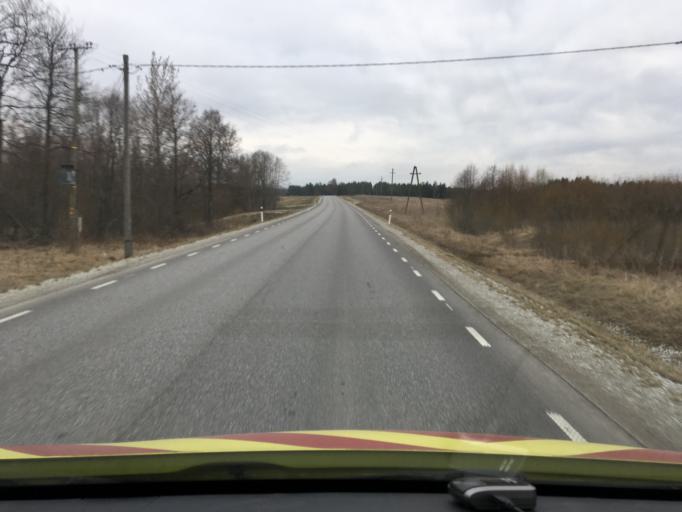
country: EE
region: Raplamaa
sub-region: Rapla vald
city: Rapla
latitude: 59.0019
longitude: 24.8426
